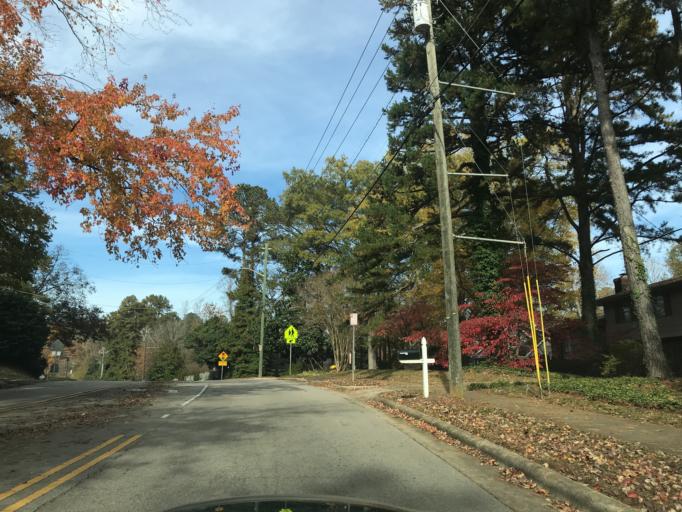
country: US
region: North Carolina
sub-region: Wake County
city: West Raleigh
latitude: 35.8118
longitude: -78.6766
